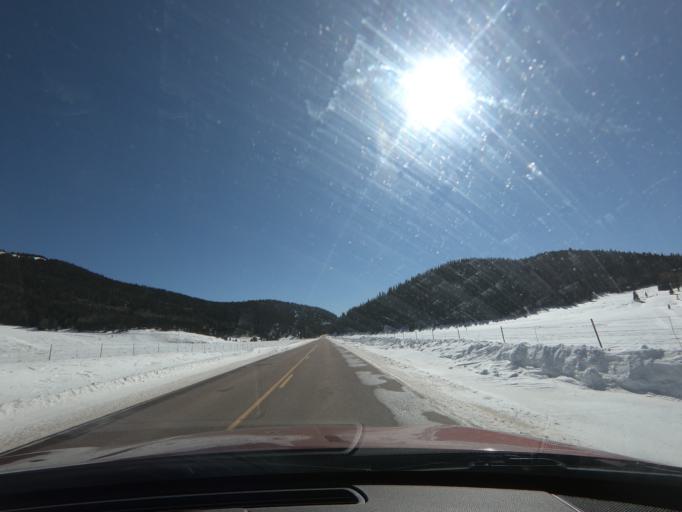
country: US
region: Colorado
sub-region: Teller County
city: Cripple Creek
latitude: 38.7580
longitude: -105.1083
